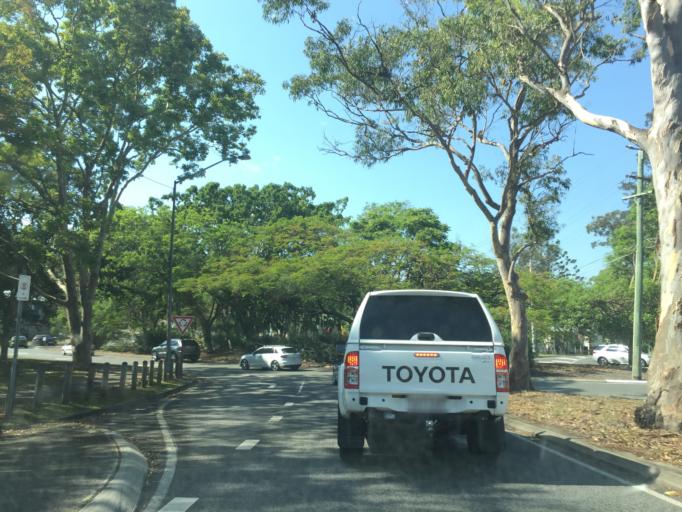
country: AU
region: Queensland
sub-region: Brisbane
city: Milton
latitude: -27.4669
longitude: 152.9878
